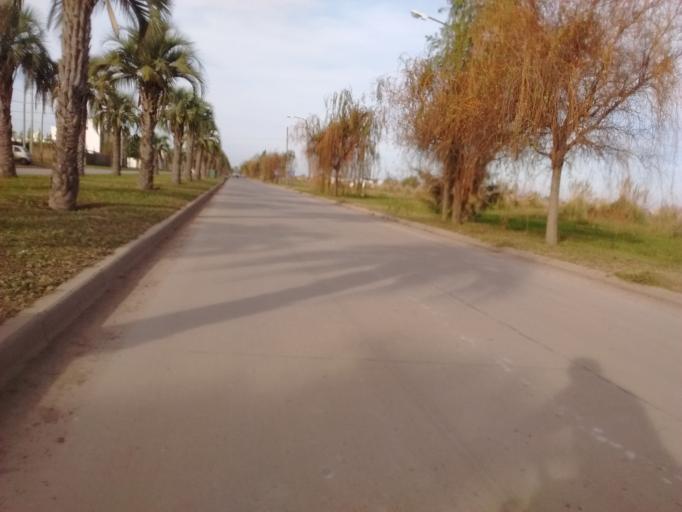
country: AR
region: Santa Fe
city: Roldan
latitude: -32.9313
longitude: -60.8987
